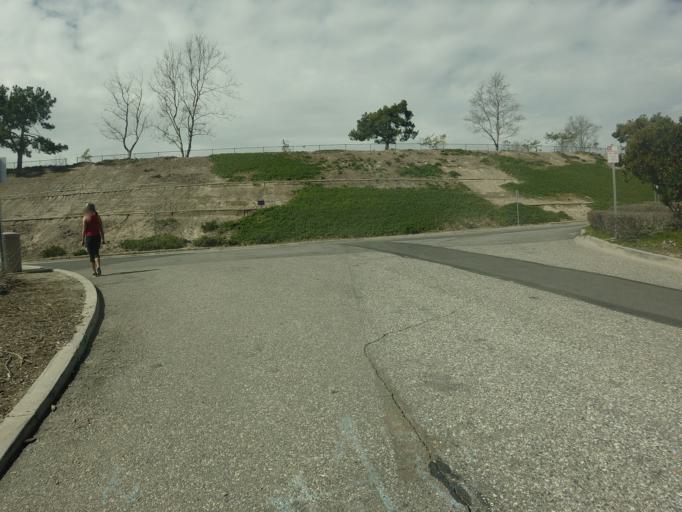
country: US
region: California
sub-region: Orange County
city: Aliso Viejo
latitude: 33.5520
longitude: -117.7210
